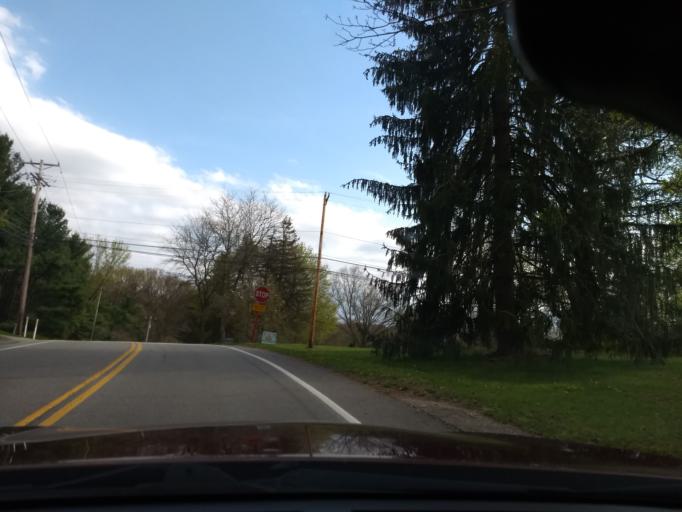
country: US
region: Pennsylvania
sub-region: Allegheny County
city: Fox Chapel
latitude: 40.5455
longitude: -79.8770
